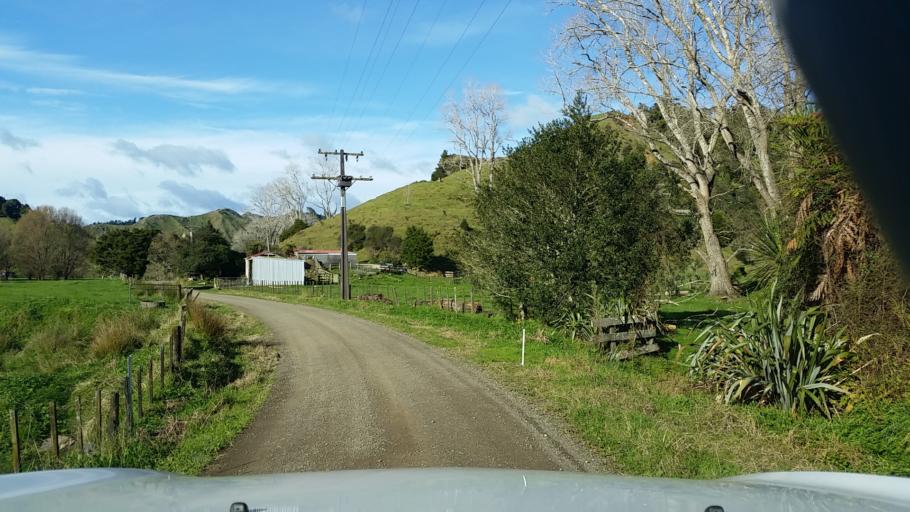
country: NZ
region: Taranaki
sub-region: New Plymouth District
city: Waitara
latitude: -38.9360
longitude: 174.5384
